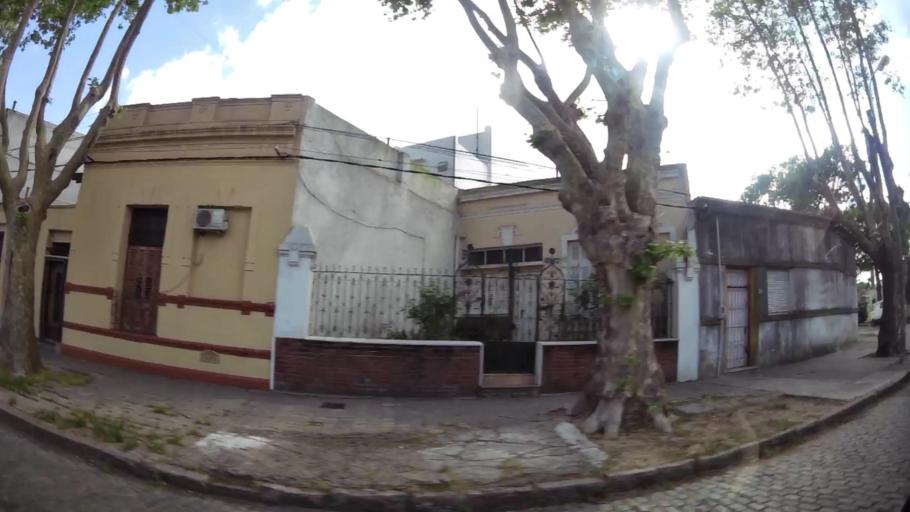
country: UY
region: Montevideo
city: Montevideo
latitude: -34.8741
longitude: -56.1758
